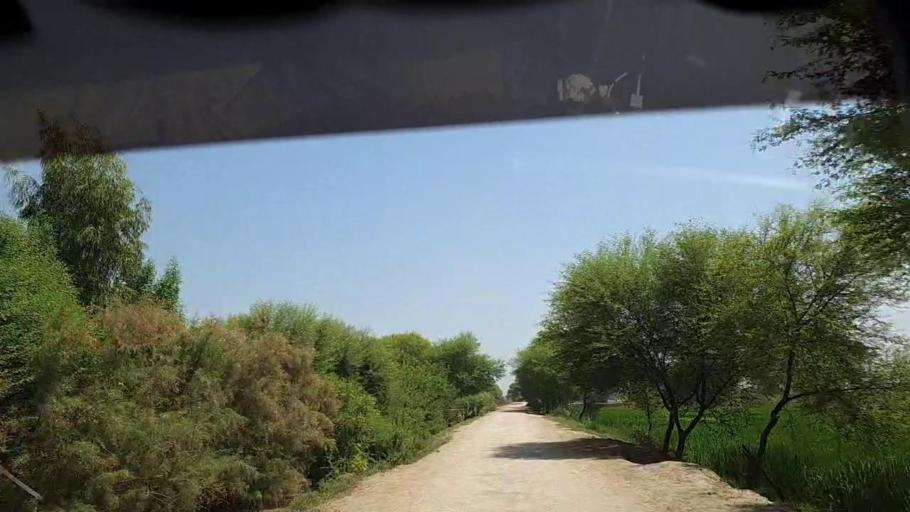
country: PK
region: Sindh
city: Ghauspur
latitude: 28.1694
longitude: 69.0682
